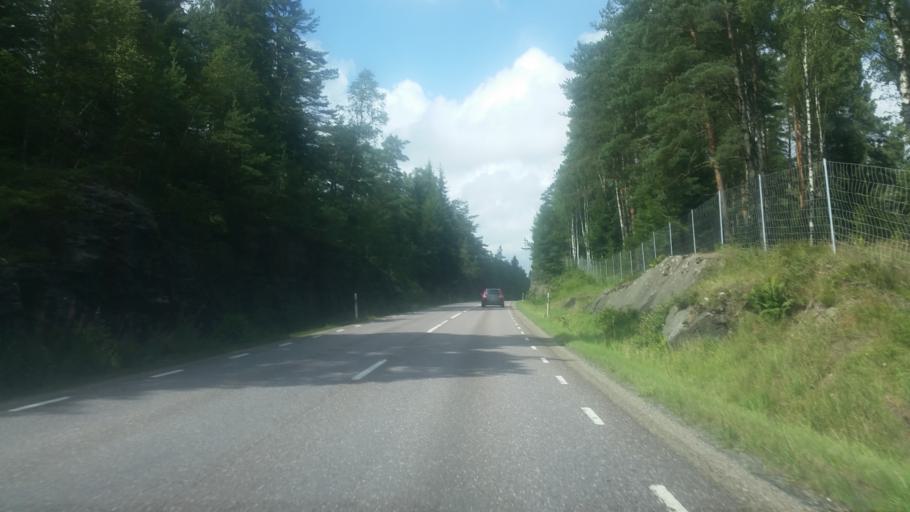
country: SE
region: Vaestra Goetaland
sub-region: Partille Kommun
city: Furulund
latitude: 57.6936
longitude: 12.1589
